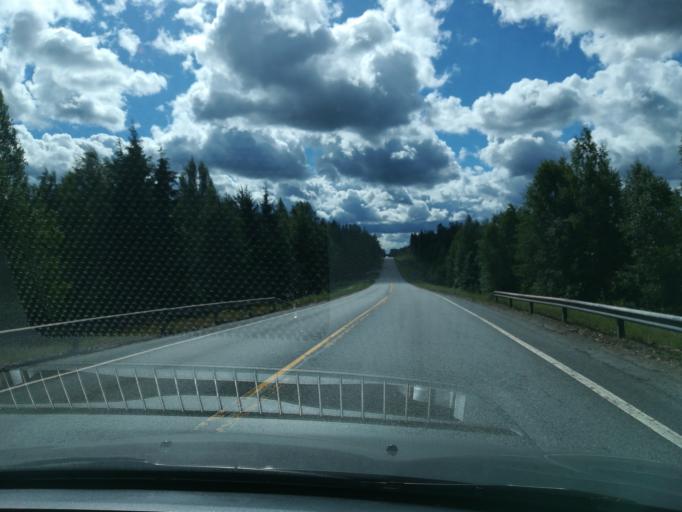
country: FI
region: Southern Savonia
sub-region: Mikkeli
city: Ristiina
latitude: 61.4595
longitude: 27.2560
